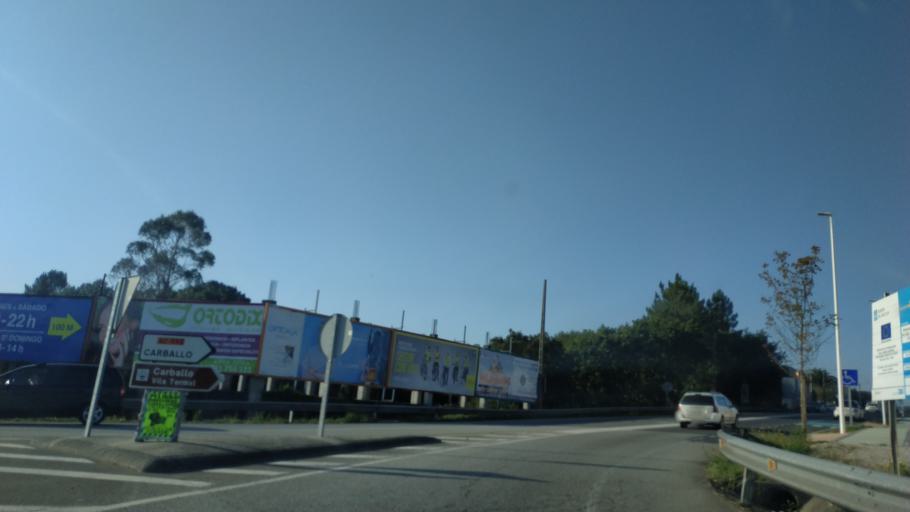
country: ES
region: Galicia
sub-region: Provincia da Coruna
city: Carballo
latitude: 43.2282
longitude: -8.6759
